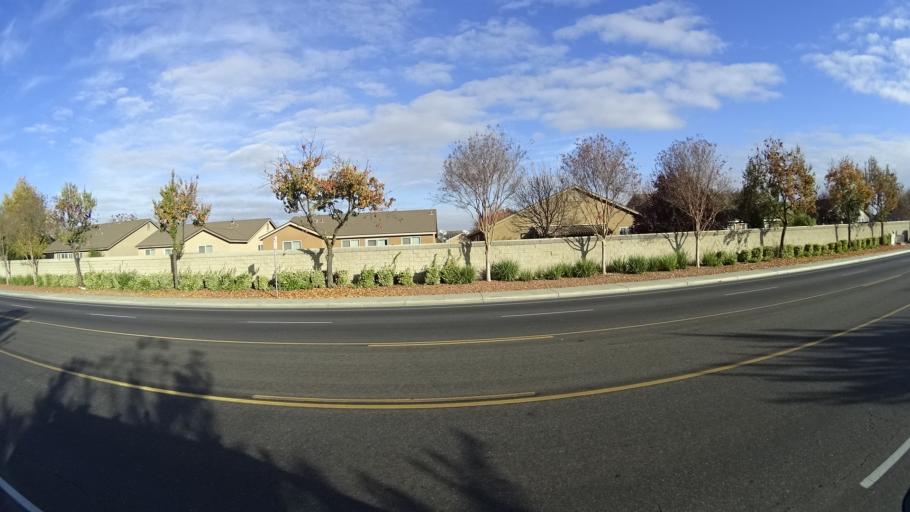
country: US
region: California
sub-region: Kern County
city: Greenacres
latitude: 35.3034
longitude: -119.1042
